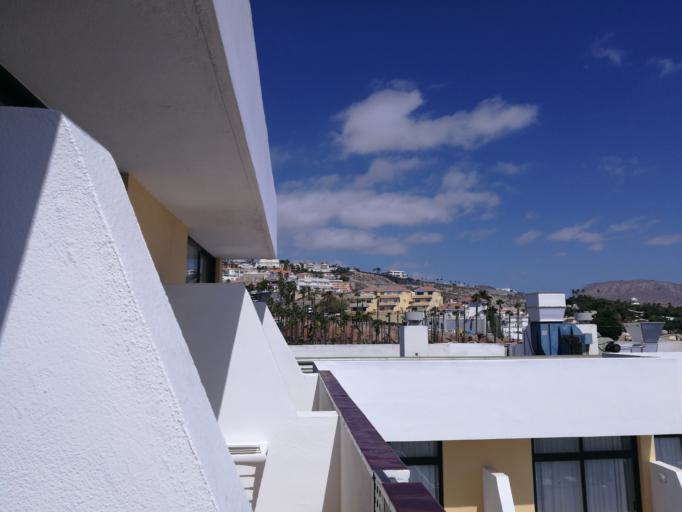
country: ES
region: Canary Islands
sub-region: Provincia de Santa Cruz de Tenerife
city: Playa de las Americas
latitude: 28.0765
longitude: -16.7304
